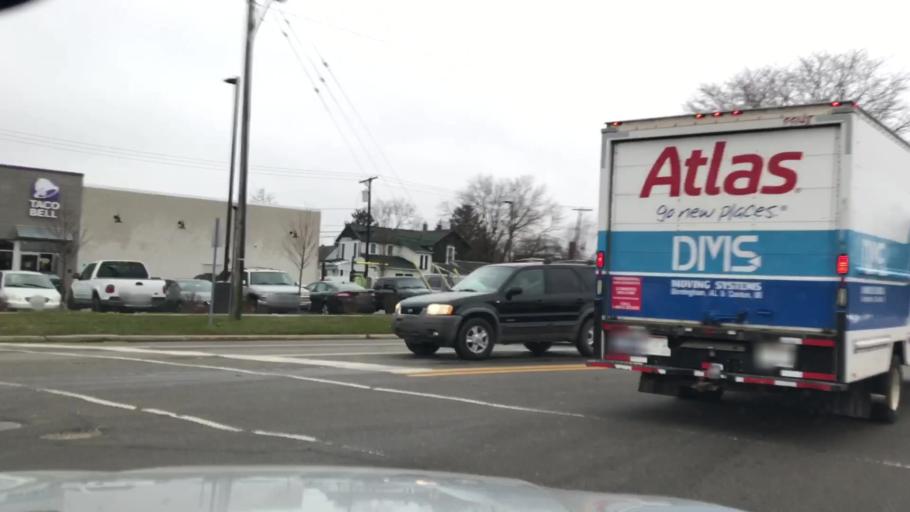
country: US
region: Michigan
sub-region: Wayne County
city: Plymouth
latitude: 42.3768
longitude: -83.4605
